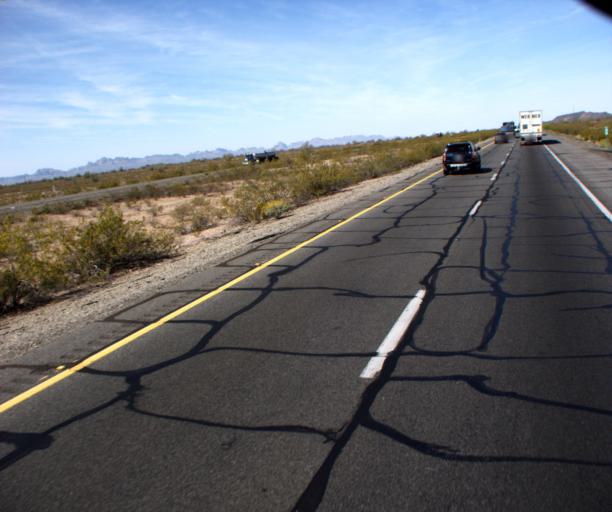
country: US
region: Arizona
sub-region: Maricopa County
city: Buckeye
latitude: 33.5159
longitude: -113.0401
